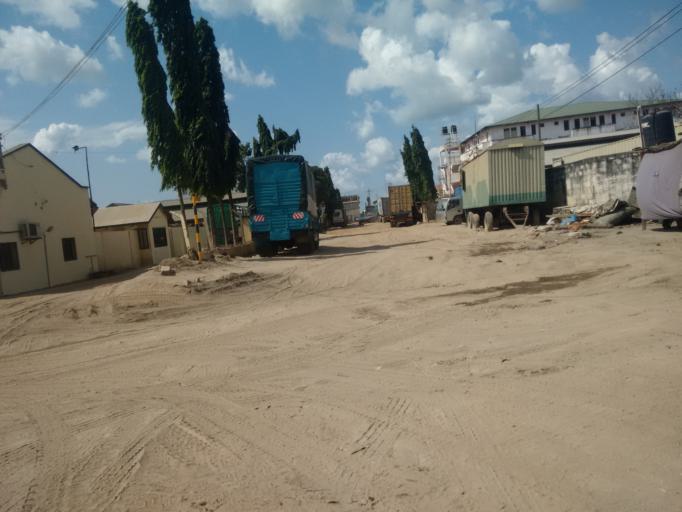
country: TZ
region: Dar es Salaam
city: Dar es Salaam
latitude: -6.8397
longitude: 39.2678
